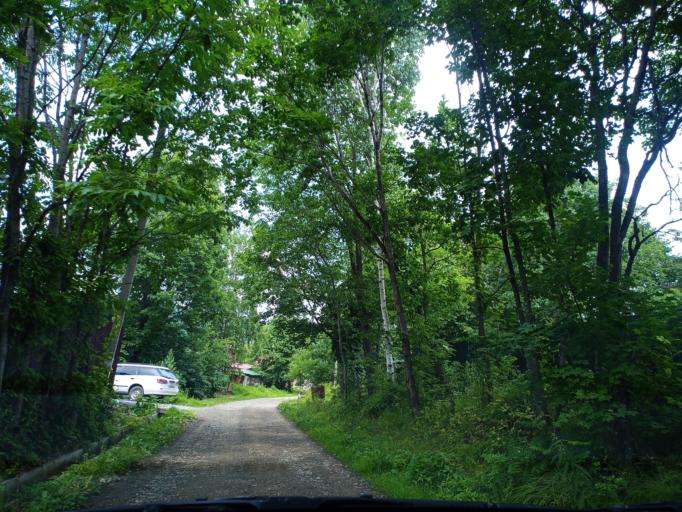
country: RU
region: Khabarovsk Krai
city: Korfovskiy
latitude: 48.3208
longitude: 135.0984
